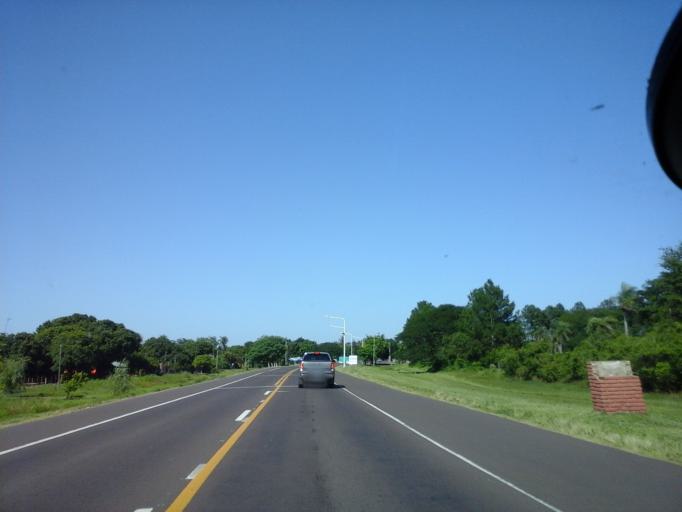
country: AR
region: Corrientes
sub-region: Departamento de San Cosme
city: San Cosme
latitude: -27.3903
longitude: -58.5524
